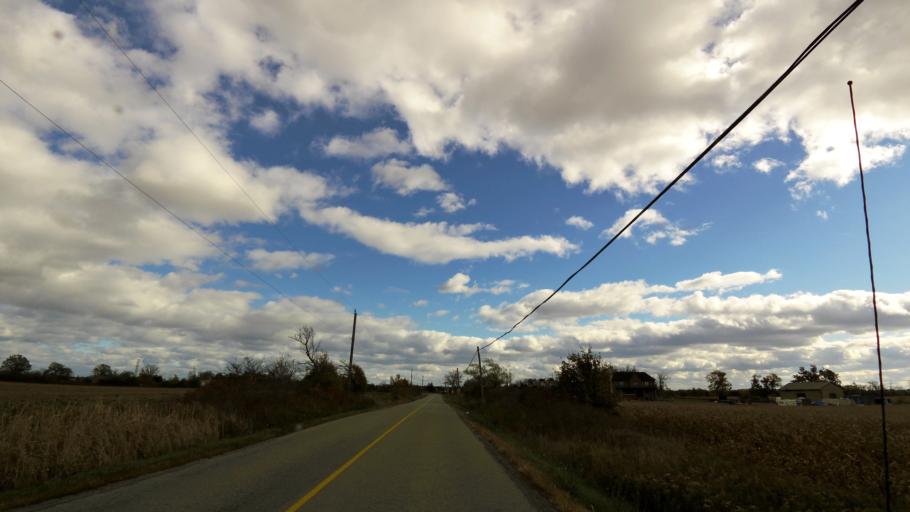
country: CA
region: Ontario
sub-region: Halton
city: Milton
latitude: 43.4884
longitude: -79.7890
